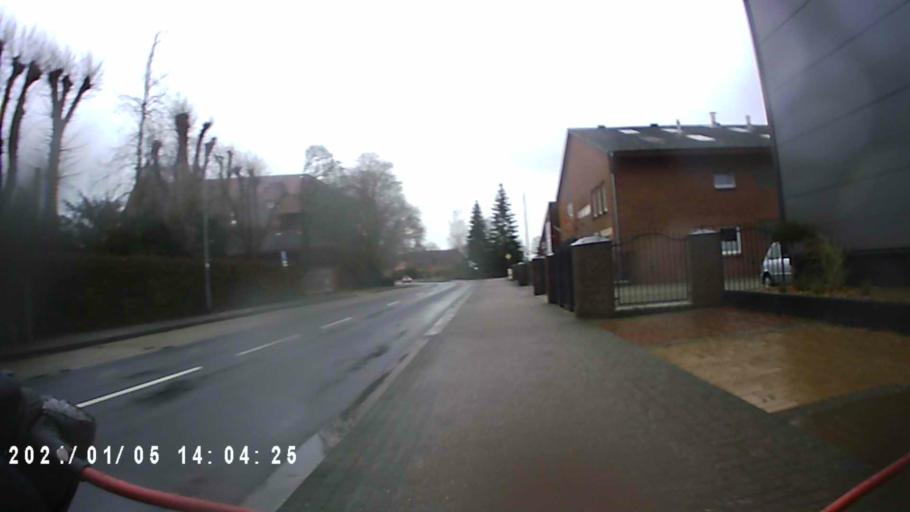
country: DE
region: Lower Saxony
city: Weener
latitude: 53.1638
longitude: 7.3461
